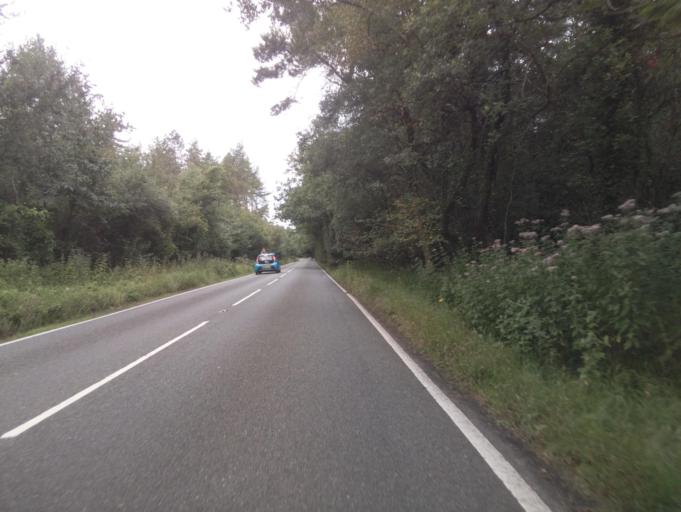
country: GB
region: England
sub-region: Devon
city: Bishopsteignton
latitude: 50.6017
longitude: -3.5493
